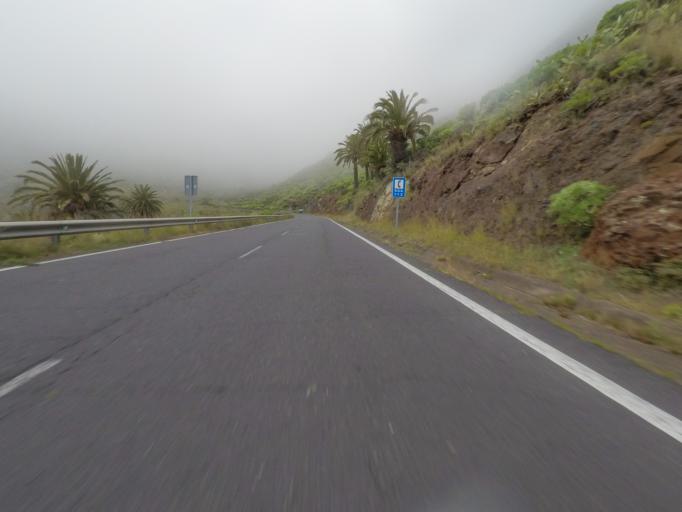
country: ES
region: Canary Islands
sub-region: Provincia de Santa Cruz de Tenerife
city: Alajero
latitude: 28.0954
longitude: -17.1996
